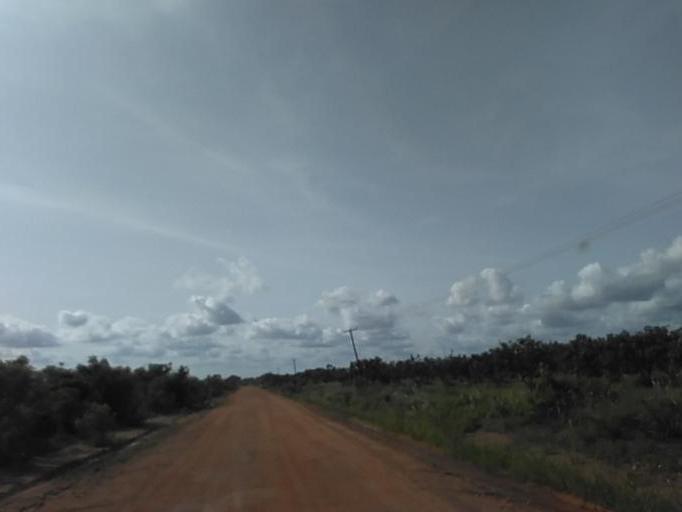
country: GH
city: Akropong
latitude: 6.0710
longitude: 0.2841
